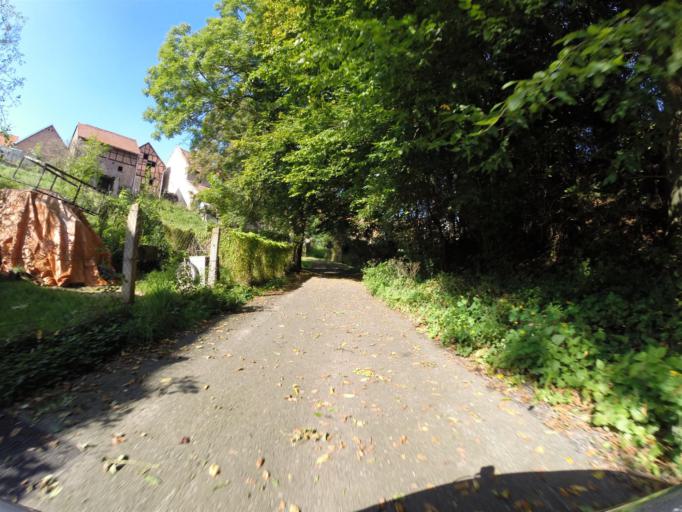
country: DE
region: Thuringia
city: Schongleina
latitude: 50.9074
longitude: 11.7263
